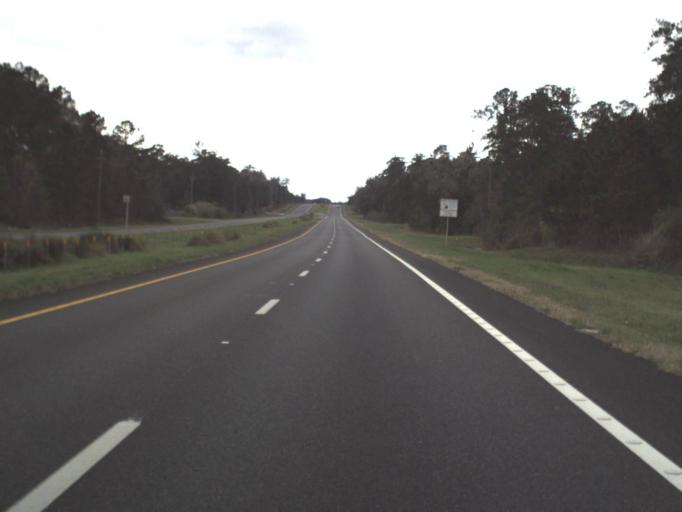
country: US
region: Florida
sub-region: Leon County
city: Tallahassee
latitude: 30.5895
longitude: -84.1932
